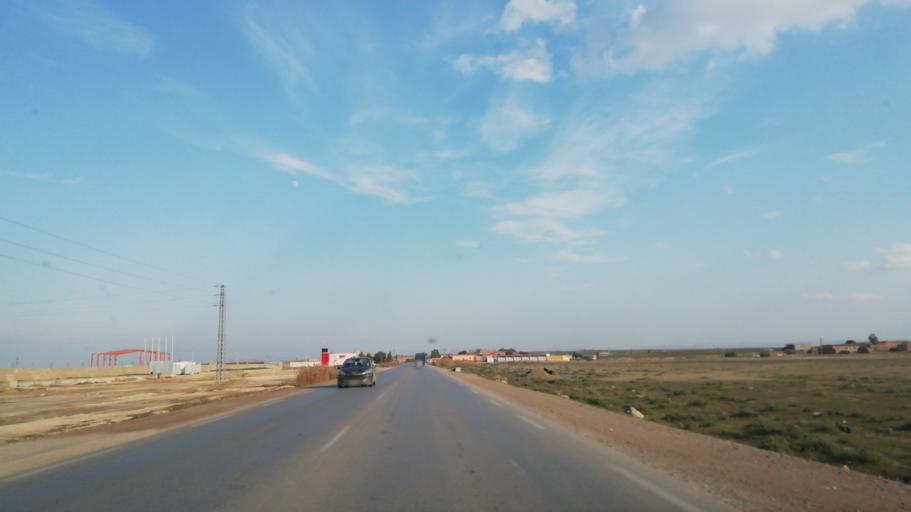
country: DZ
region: Relizane
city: Relizane
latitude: 35.8980
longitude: 0.5823
